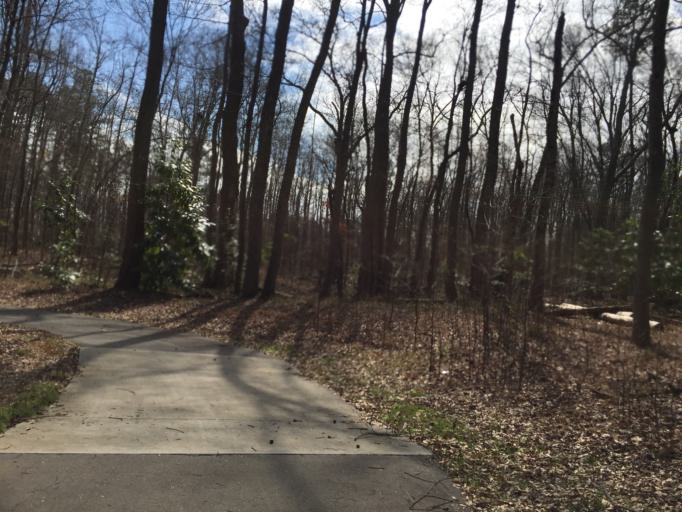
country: US
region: South Carolina
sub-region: Greenville County
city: Mauldin
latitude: 34.7898
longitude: -82.3653
